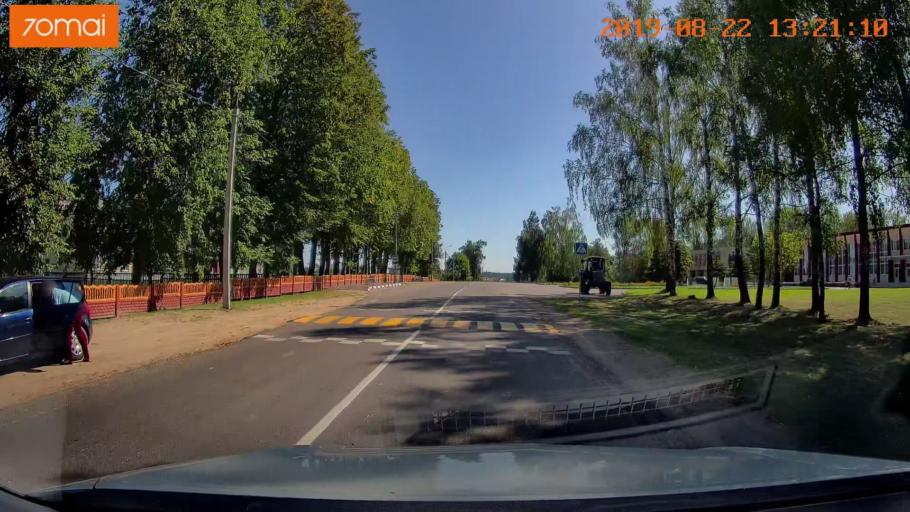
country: BY
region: Minsk
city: Urechcha
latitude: 53.2258
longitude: 27.9779
